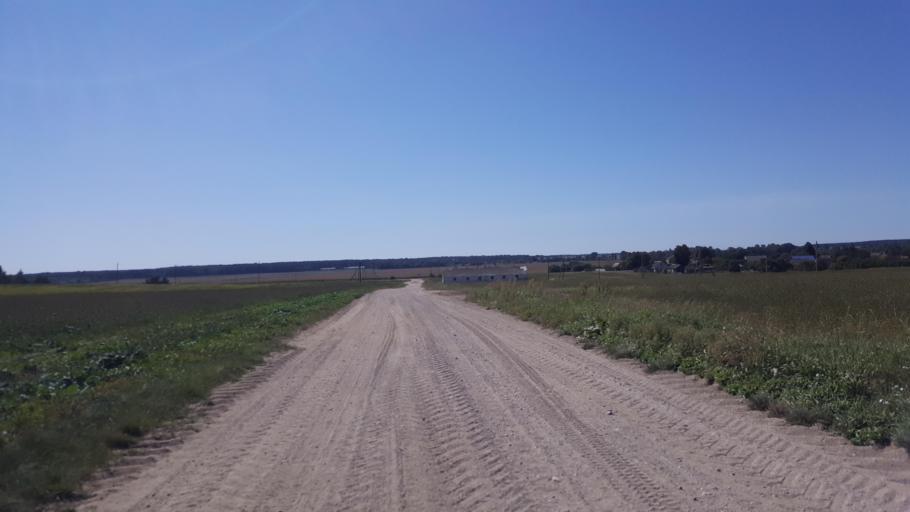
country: PL
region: Lublin Voivodeship
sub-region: Powiat bialski
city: Terespol
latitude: 52.2165
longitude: 23.5181
